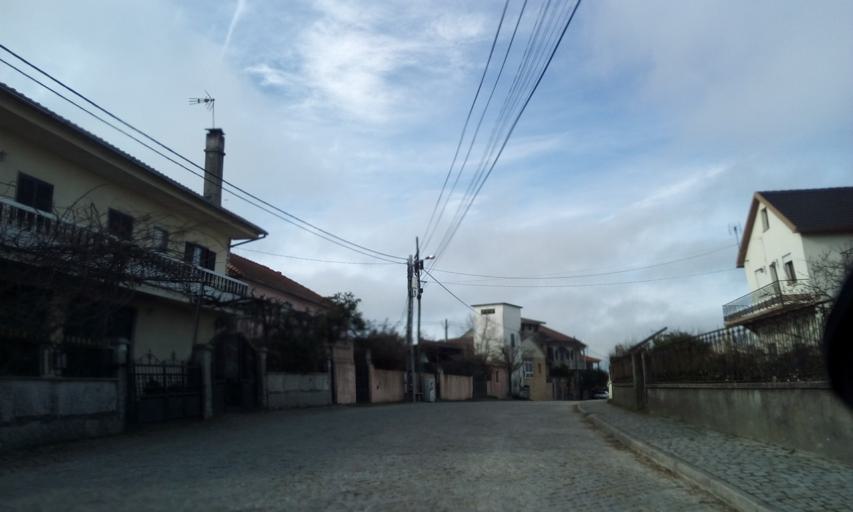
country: PT
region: Guarda
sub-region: Aguiar da Beira
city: Aguiar da Beira
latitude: 40.7656
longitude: -7.5378
